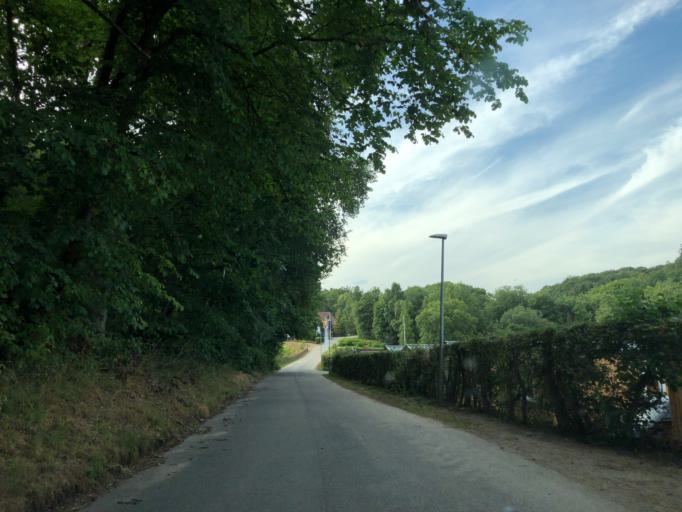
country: DK
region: South Denmark
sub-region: Vejle Kommune
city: Egtved
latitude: 55.6889
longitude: 9.2683
